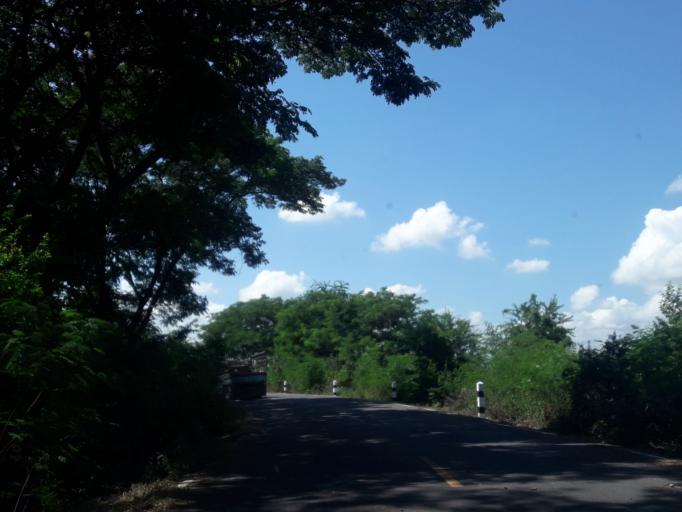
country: TH
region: Lop Buri
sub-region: Amphoe Tha Luang
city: Tha Luang
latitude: 15.0695
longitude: 101.0334
